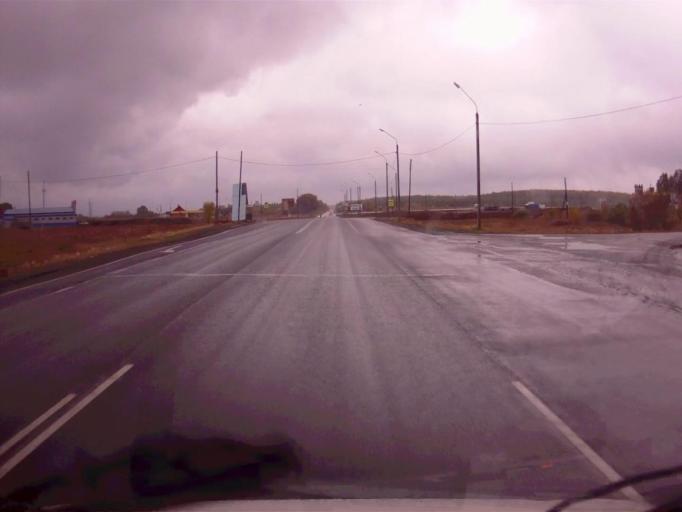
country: RU
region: Chelyabinsk
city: Tayginka
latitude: 55.4986
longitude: 60.6398
